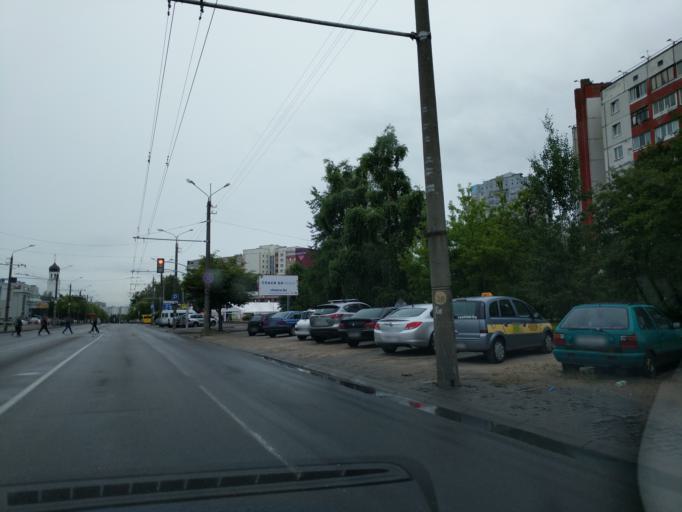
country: BY
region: Minsk
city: Novoye Medvezhino
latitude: 53.8624
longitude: 27.4792
